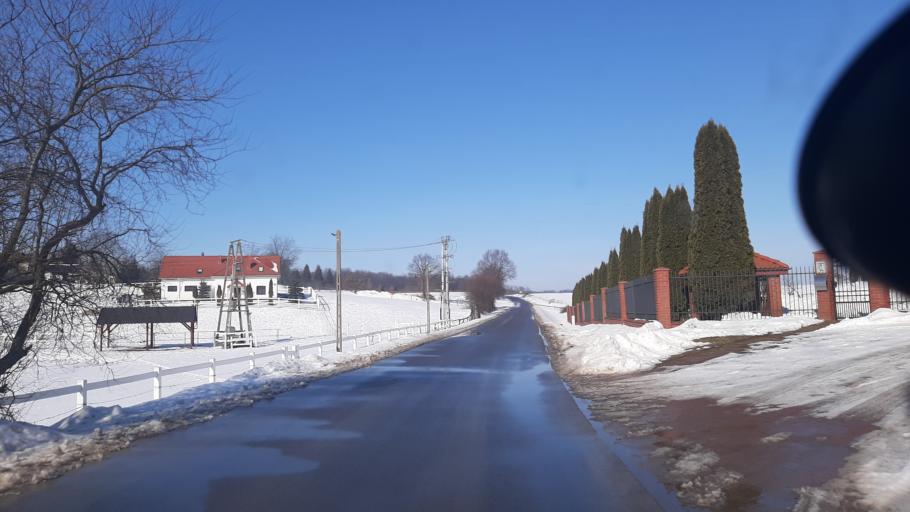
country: PL
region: Lublin Voivodeship
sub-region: Powiat pulawski
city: Naleczow
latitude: 51.2897
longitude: 22.2726
